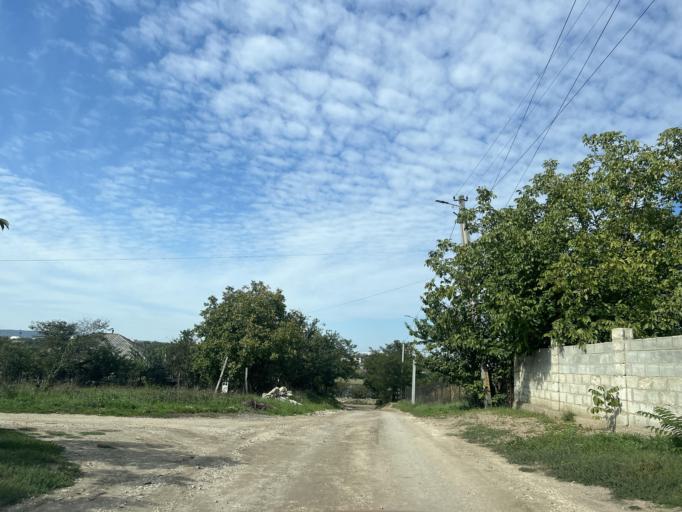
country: MD
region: Ungheni
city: Ungheni
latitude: 47.2037
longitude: 27.8134
